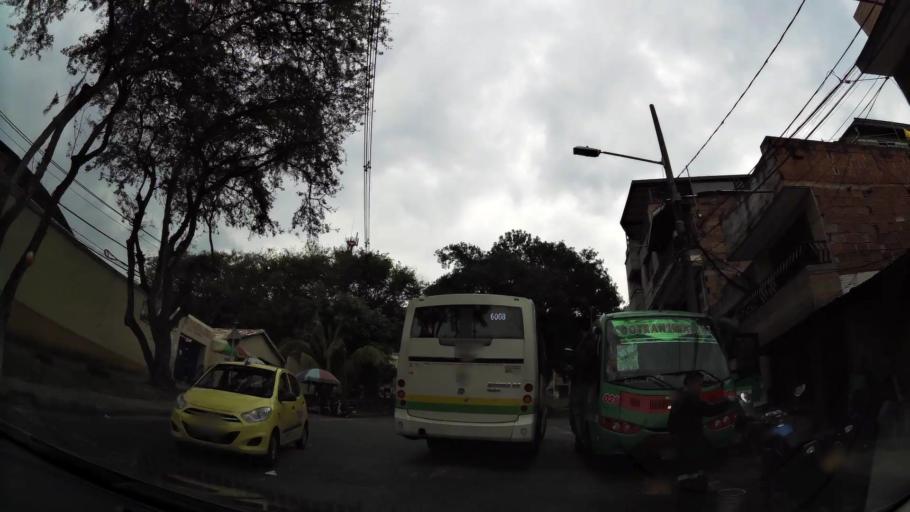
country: CO
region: Antioquia
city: Medellin
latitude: 6.2496
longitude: -75.5490
